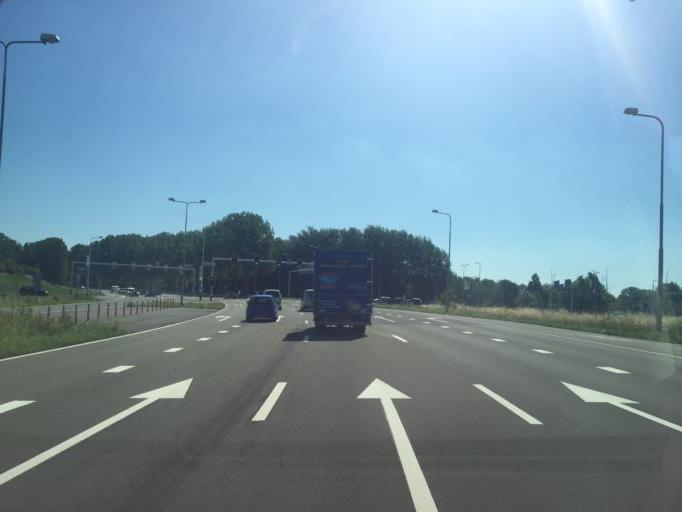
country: NL
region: North Holland
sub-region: Gemeente Haarlemmermeer
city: Hoofddorp
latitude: 52.3159
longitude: 4.6741
